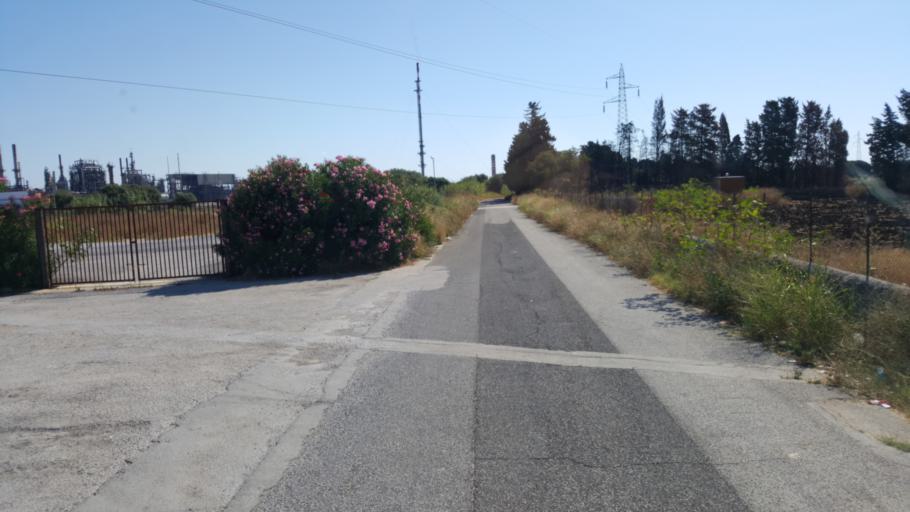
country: IT
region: Sicily
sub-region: Provincia di Siracusa
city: Melilli
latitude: 37.2053
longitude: 15.1663
